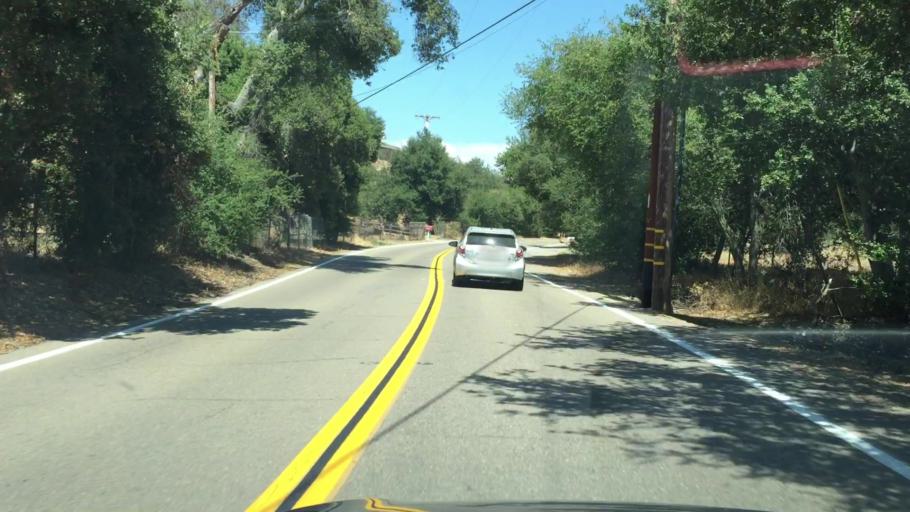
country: US
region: California
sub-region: San Diego County
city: Jamul
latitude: 32.7430
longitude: -116.8078
